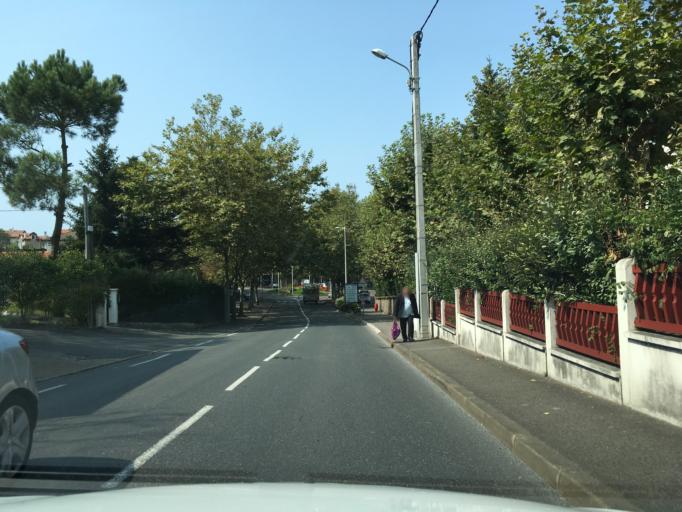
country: FR
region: Aquitaine
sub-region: Departement des Pyrenees-Atlantiques
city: Biarritz
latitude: 43.4961
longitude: -1.5369
